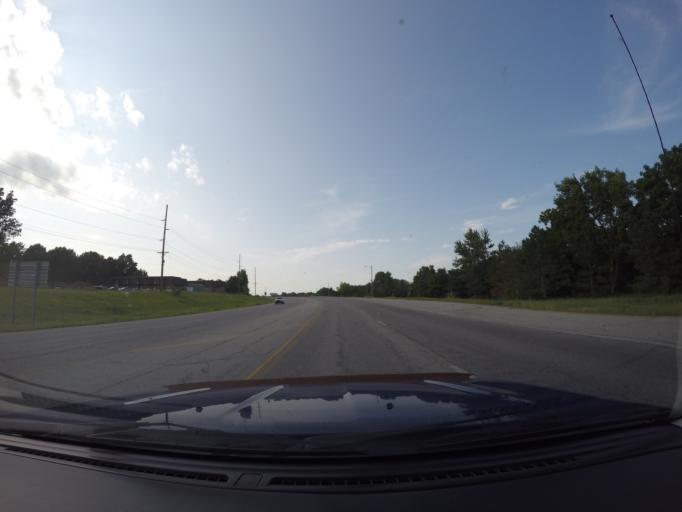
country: US
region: Kansas
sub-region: Riley County
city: Manhattan
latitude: 39.1984
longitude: -96.6125
